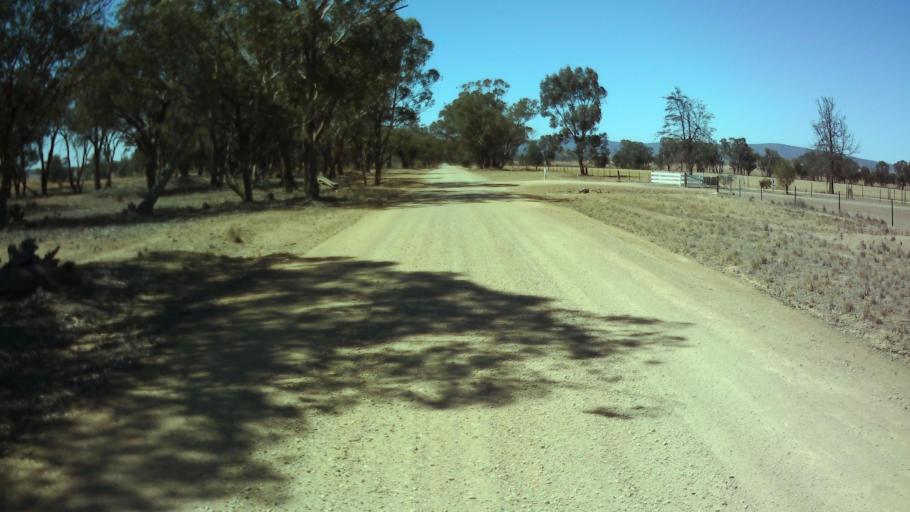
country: AU
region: New South Wales
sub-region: Weddin
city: Grenfell
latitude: -33.8664
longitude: 148.0877
